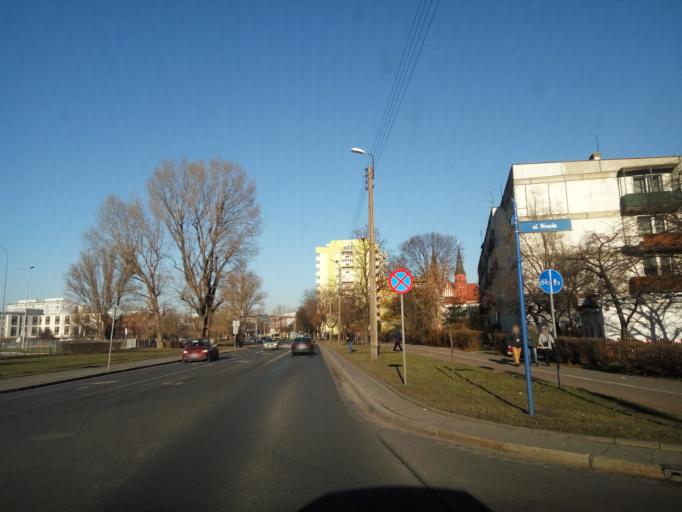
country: PL
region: Lower Silesian Voivodeship
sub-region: Powiat wroclawski
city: Wroclaw
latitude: 51.0915
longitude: 17.0339
